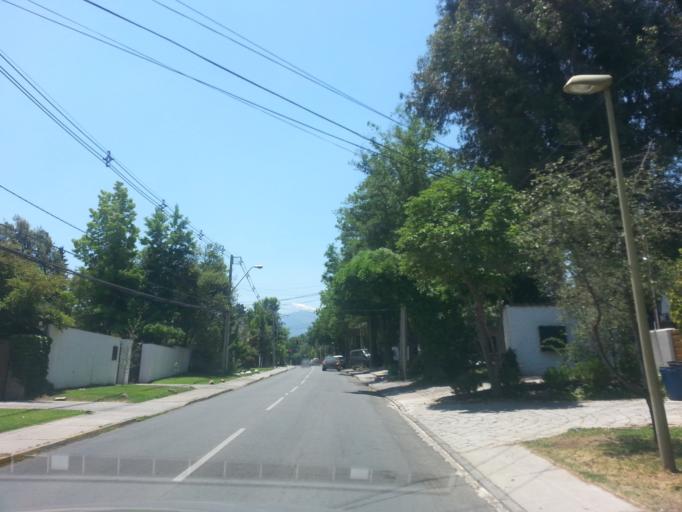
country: CL
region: Santiago Metropolitan
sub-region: Provincia de Santiago
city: Villa Presidente Frei, Nunoa, Santiago, Chile
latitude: -33.3917
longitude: -70.5274
